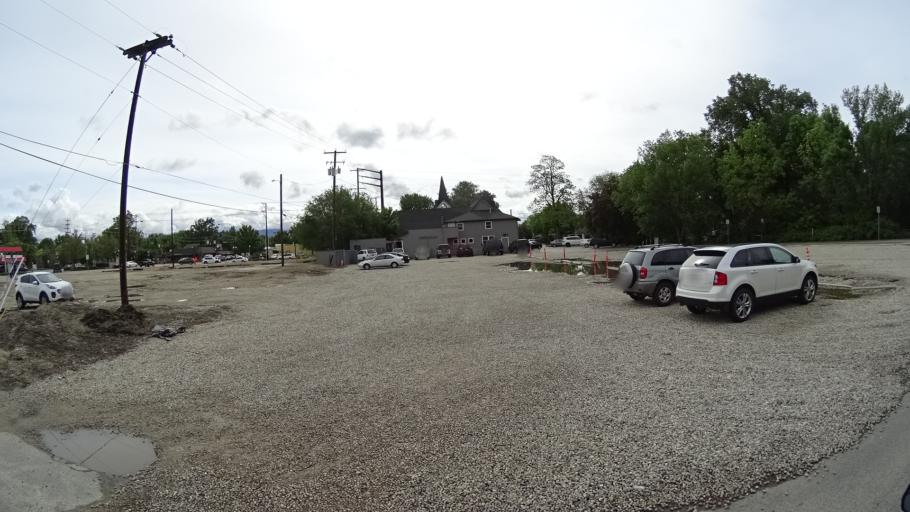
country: US
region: Idaho
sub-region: Ada County
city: Eagle
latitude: 43.6946
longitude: -116.3556
